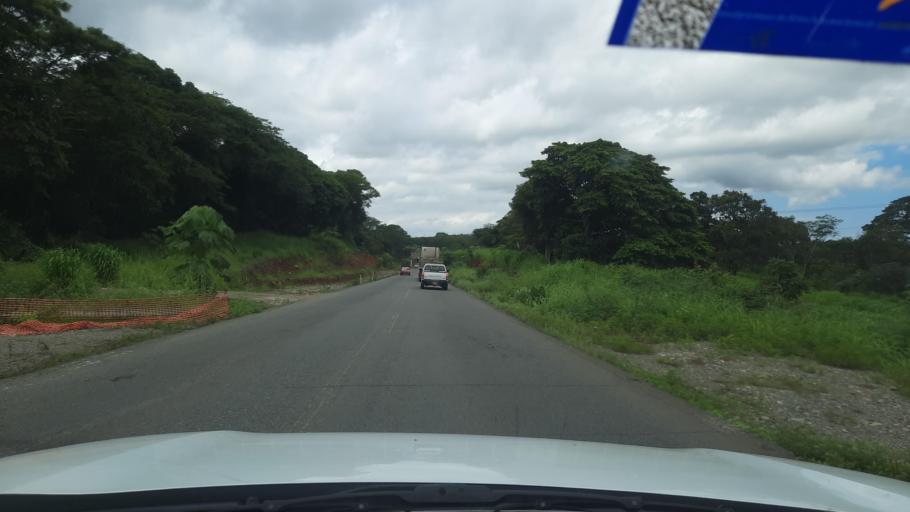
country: CR
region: Puntarenas
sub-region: Canton Central de Puntarenas
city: Puntarenas
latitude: 10.1048
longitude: -84.8777
